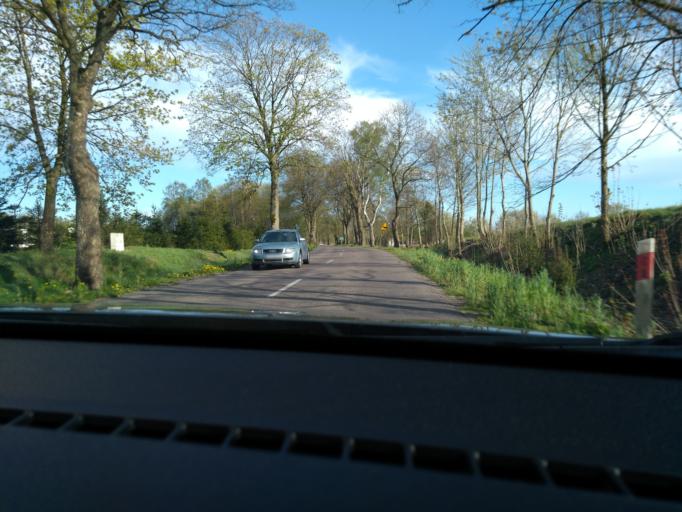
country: PL
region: Pomeranian Voivodeship
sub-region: Powiat leborski
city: Cewice
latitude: 54.3367
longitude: 17.7643
